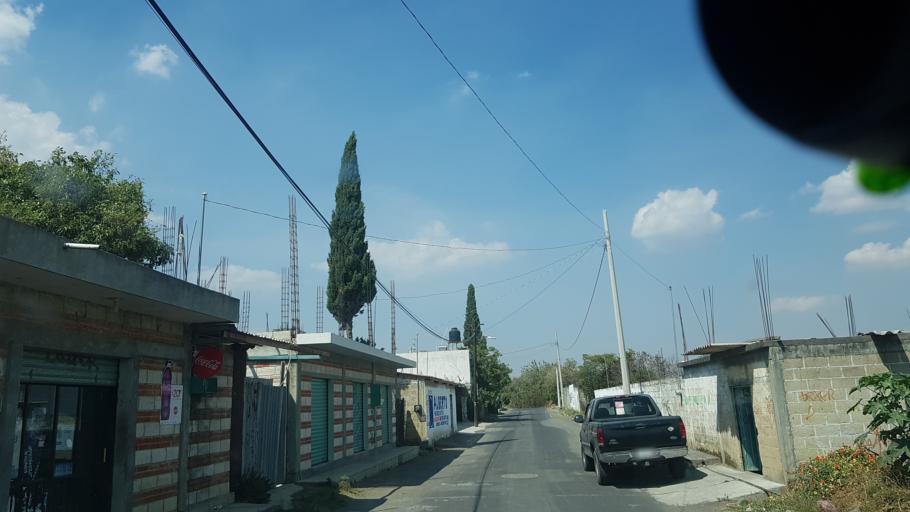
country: MX
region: Puebla
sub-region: Atlixco
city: San Pedro Benito Juarez
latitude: 18.9460
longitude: -98.5509
